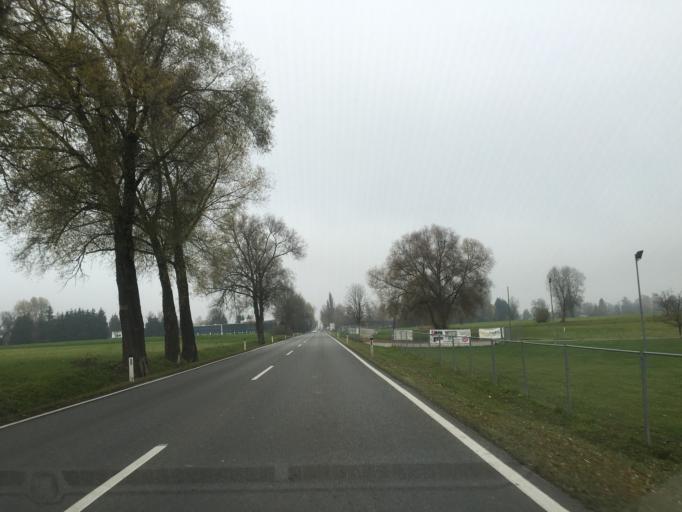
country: AT
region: Vorarlberg
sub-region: Politischer Bezirk Dornbirn
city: Lustenau
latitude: 47.4094
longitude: 9.6697
